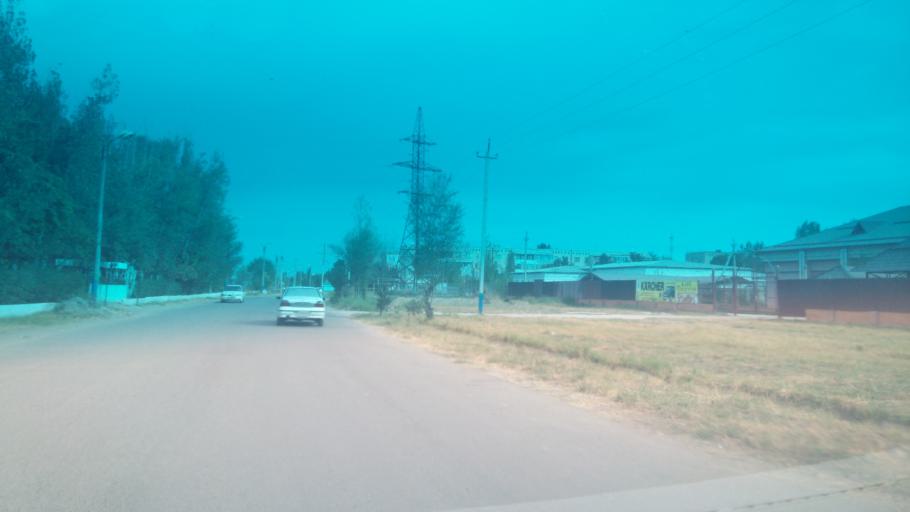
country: UZ
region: Sirdaryo
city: Guliston
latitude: 40.5124
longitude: 68.7772
